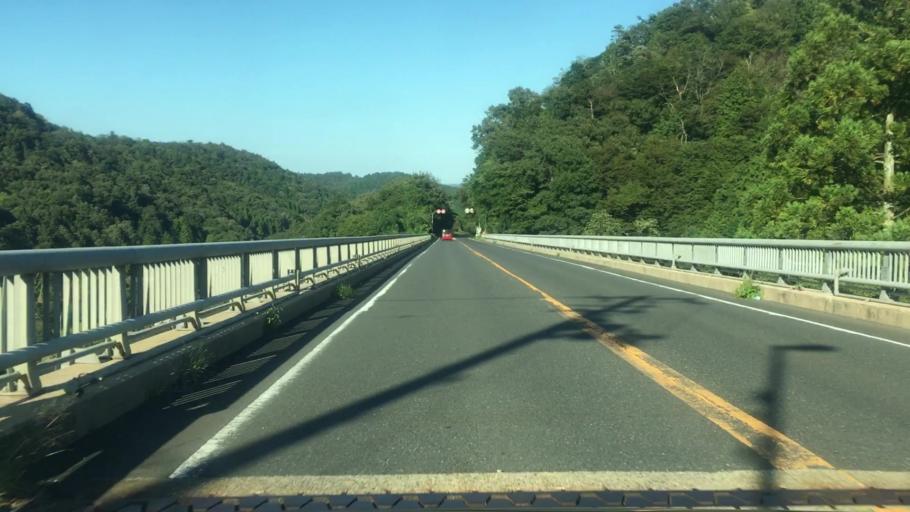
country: JP
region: Hyogo
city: Toyooka
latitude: 35.5878
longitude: 134.8689
